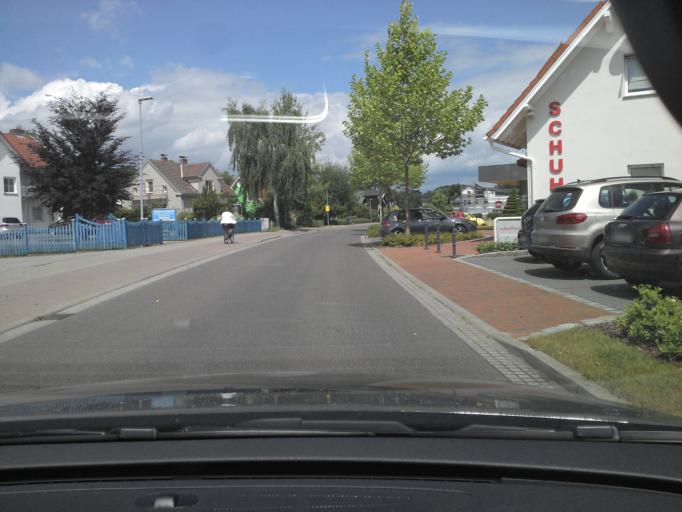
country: DE
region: Brandenburg
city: Burg
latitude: 51.8327
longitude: 14.1452
